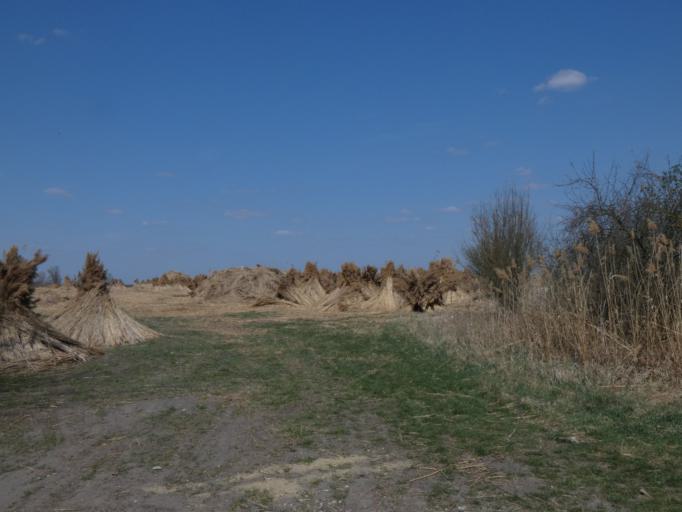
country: HU
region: Pest
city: Farmos
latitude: 47.3730
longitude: 19.8126
